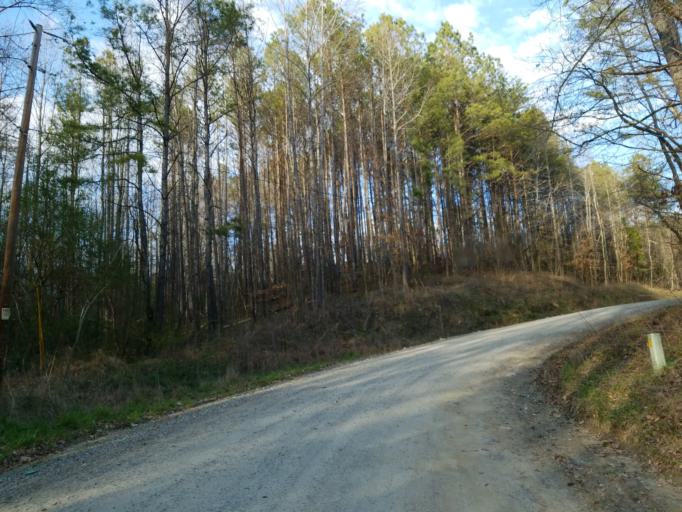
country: US
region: Georgia
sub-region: Bartow County
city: Rydal
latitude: 34.5041
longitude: -84.6334
